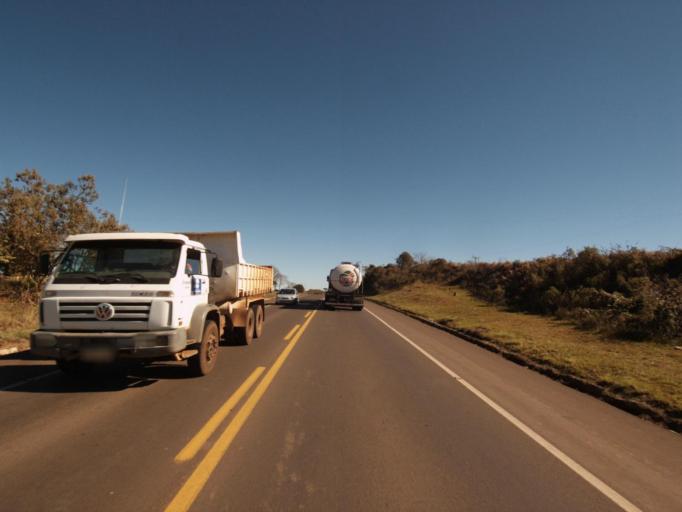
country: BR
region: Santa Catarina
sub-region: Xanxere
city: Xanxere
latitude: -26.8743
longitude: -52.3243
